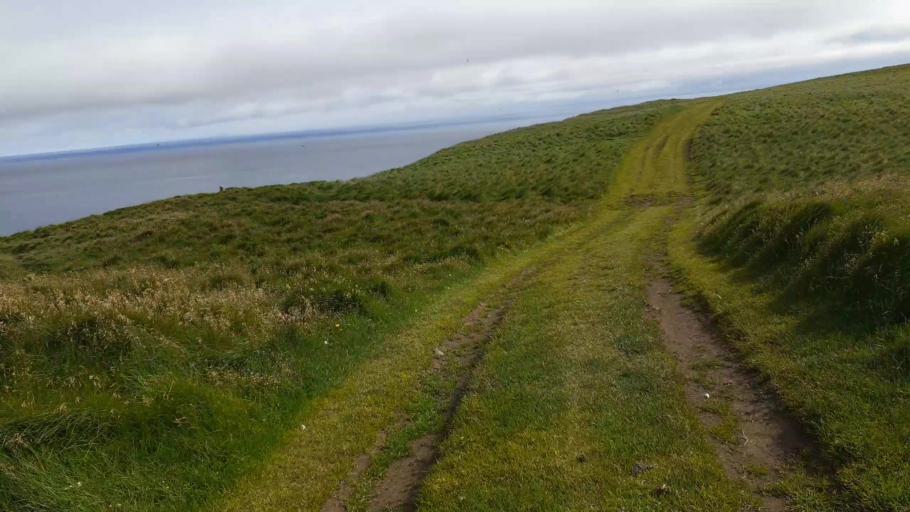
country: IS
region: Northeast
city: Dalvik
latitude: 66.5513
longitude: -17.9942
